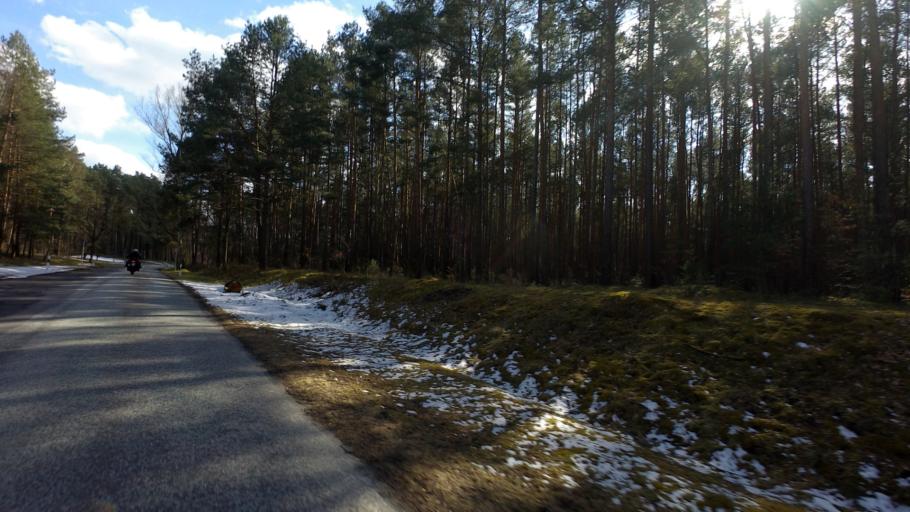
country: DE
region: Brandenburg
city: Biesenthal
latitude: 52.7799
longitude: 13.6135
